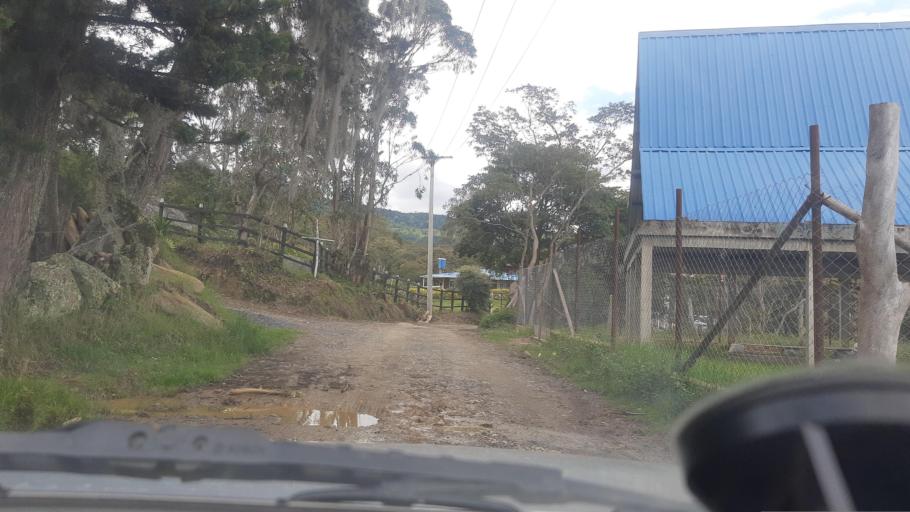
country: CO
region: Boyaca
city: Santa Sofia
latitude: 5.7933
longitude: -73.6057
